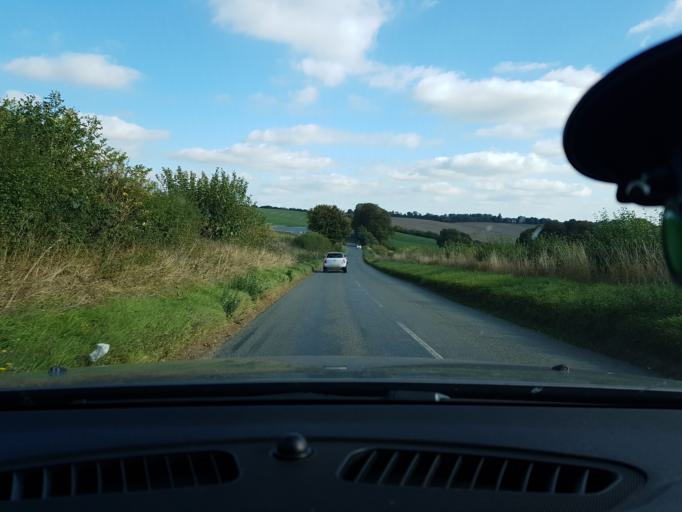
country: GB
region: England
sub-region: Wiltshire
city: Aldbourne
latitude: 51.5070
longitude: -1.6147
